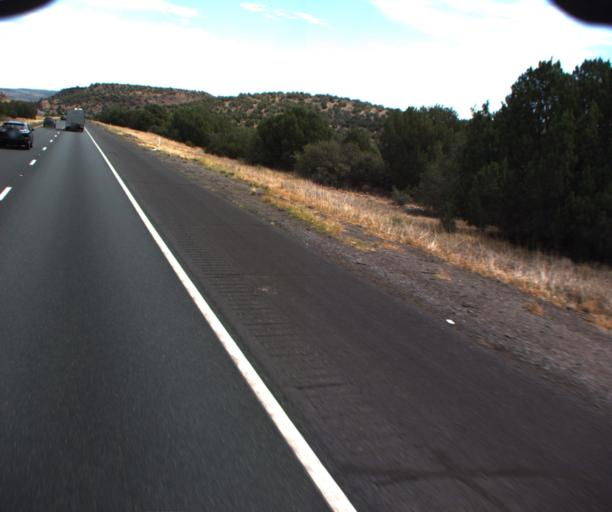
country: US
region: Arizona
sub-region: Yavapai County
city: Camp Verde
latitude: 34.4903
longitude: -112.0077
